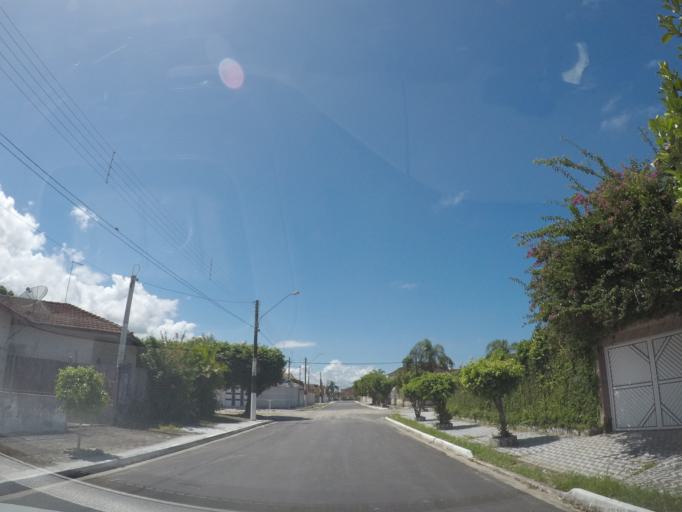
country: BR
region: Sao Paulo
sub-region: Mongagua
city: Mongagua
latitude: -24.0660
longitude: -46.5651
